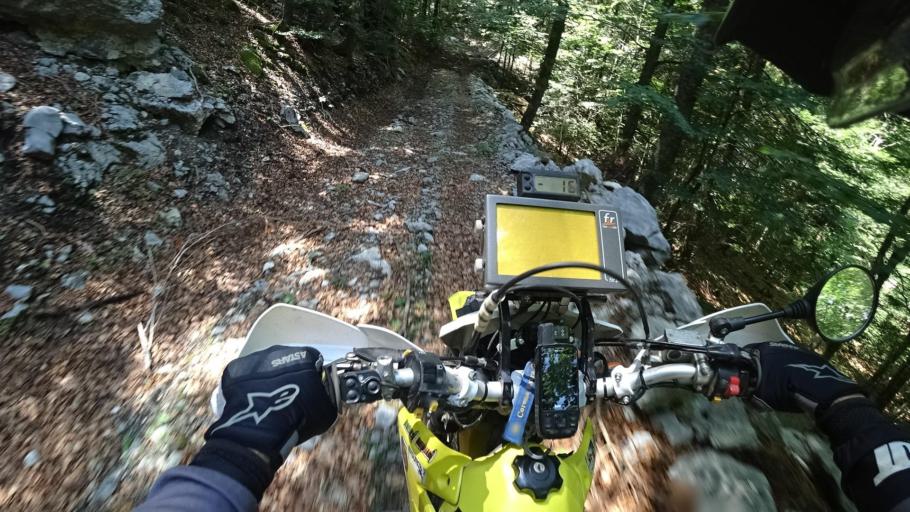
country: HR
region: Primorsko-Goranska
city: Bribir
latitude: 45.2697
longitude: 14.8409
